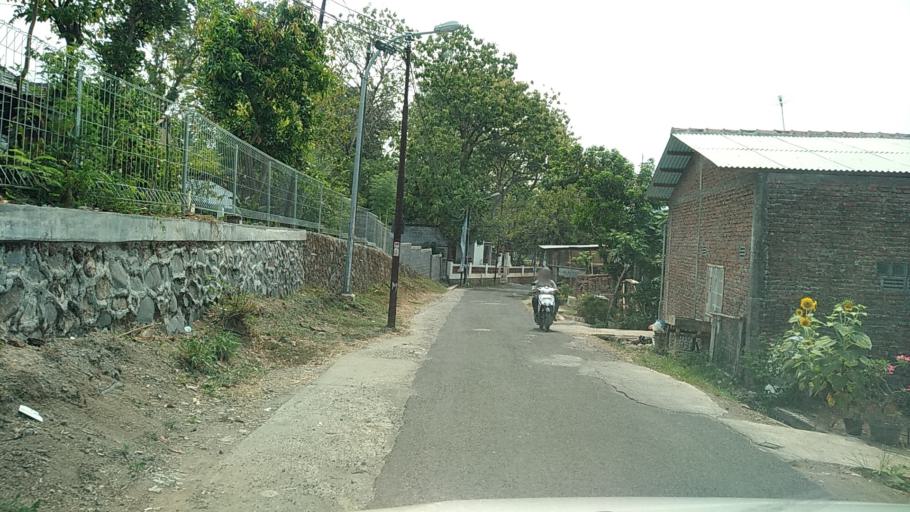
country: ID
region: Central Java
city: Semarang
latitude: -6.9968
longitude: 110.3342
